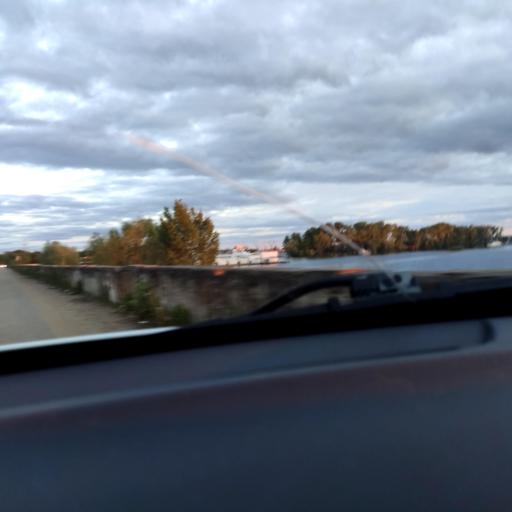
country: RU
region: Tatarstan
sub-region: Gorod Kazan'
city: Kazan
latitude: 55.7864
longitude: 49.0973
